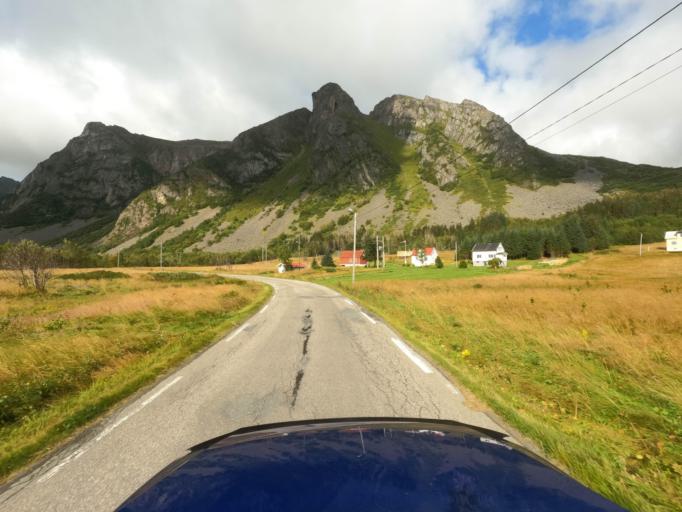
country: NO
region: Nordland
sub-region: Vestvagoy
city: Evjen
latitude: 68.2012
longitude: 13.9947
